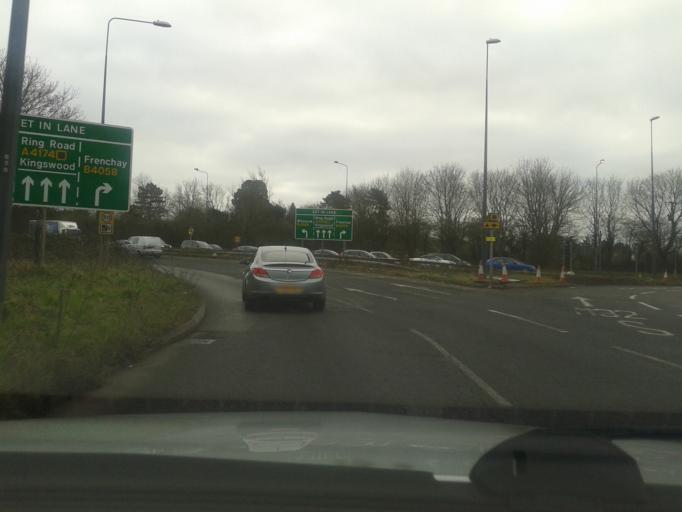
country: GB
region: England
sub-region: South Gloucestershire
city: Stoke Gifford
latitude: 51.5053
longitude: -2.5262
